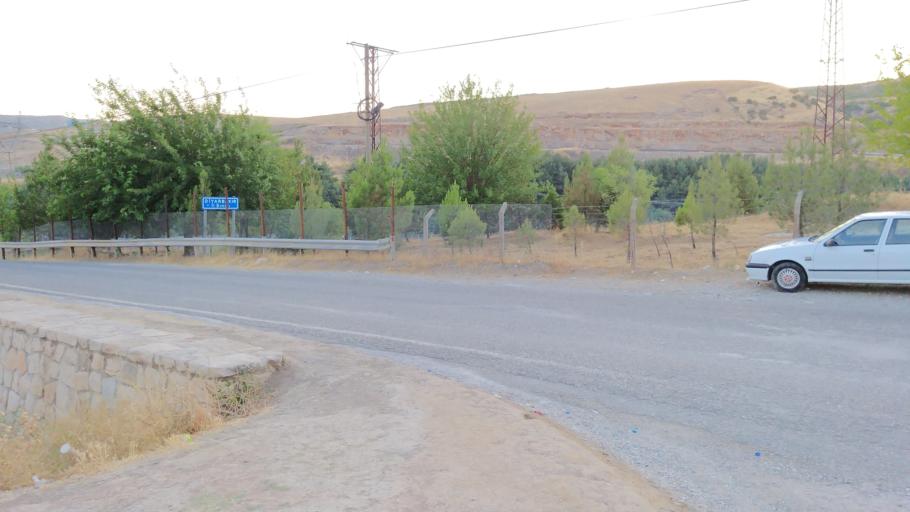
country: TR
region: Diyarbakir
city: Malabadi
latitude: 38.1544
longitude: 41.2044
